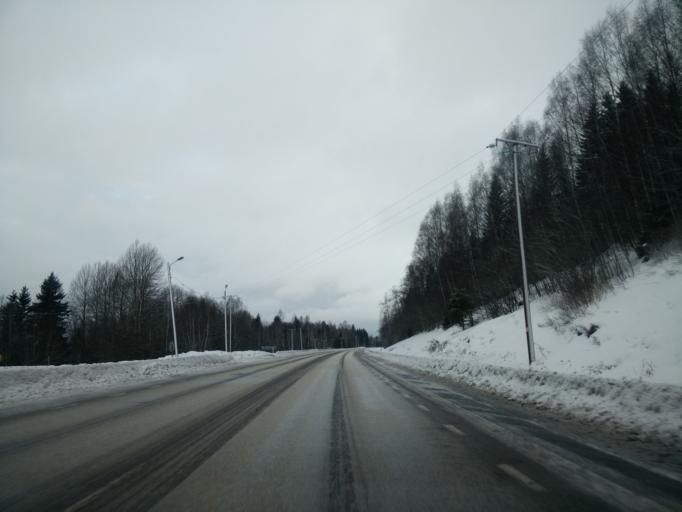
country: SE
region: Vaesternorrland
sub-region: Sundsvalls Kommun
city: Matfors
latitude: 62.3828
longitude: 16.8113
